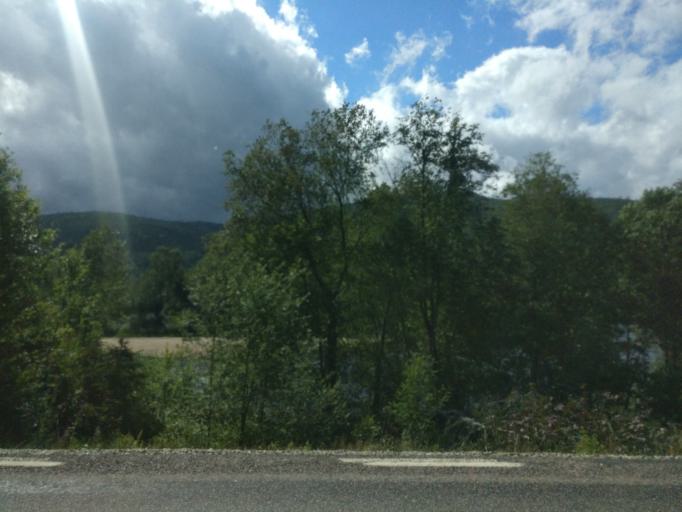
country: SE
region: Vaermland
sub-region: Hagfors Kommun
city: Ekshaerad
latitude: 60.3603
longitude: 13.3172
